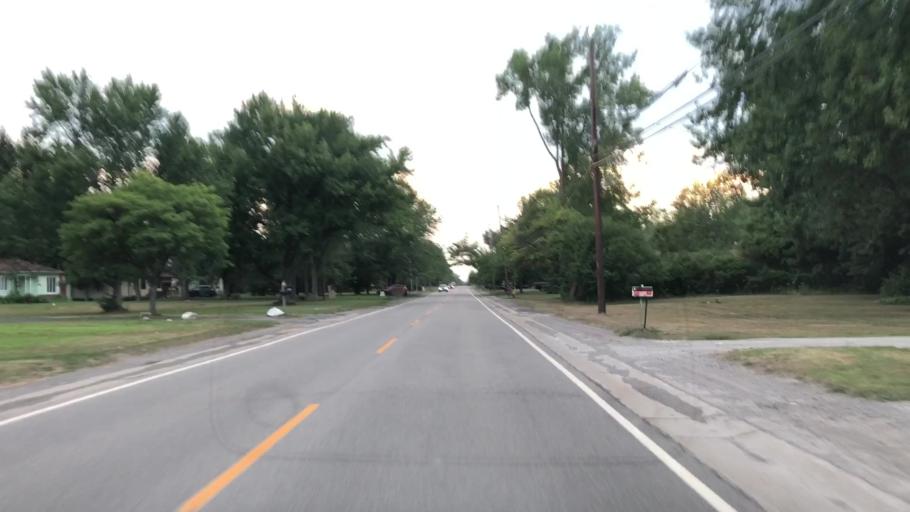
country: US
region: New York
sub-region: Erie County
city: Elma Center
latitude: 42.8393
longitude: -78.6402
